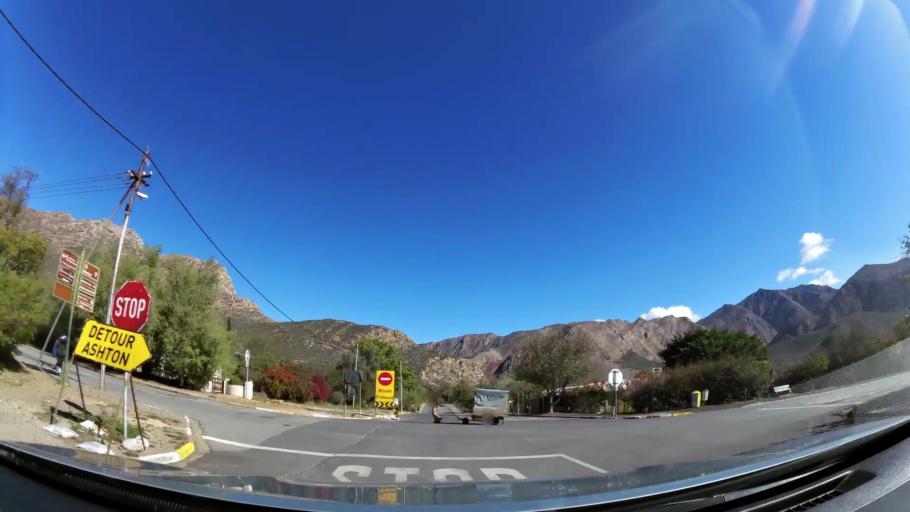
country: ZA
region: Western Cape
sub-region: Cape Winelands District Municipality
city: Ashton
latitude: -33.7934
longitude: 20.1209
